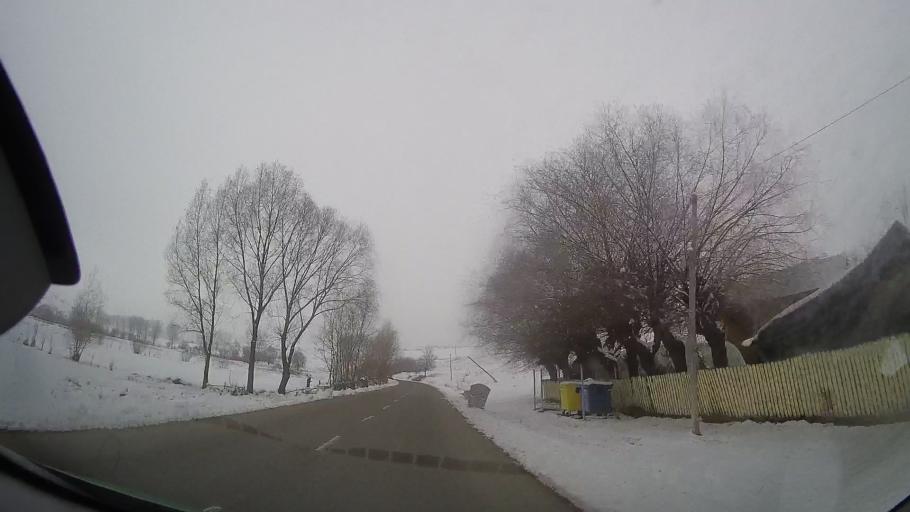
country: RO
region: Neamt
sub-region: Comuna Oniceni
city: Oniceni
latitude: 46.8012
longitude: 27.1374
